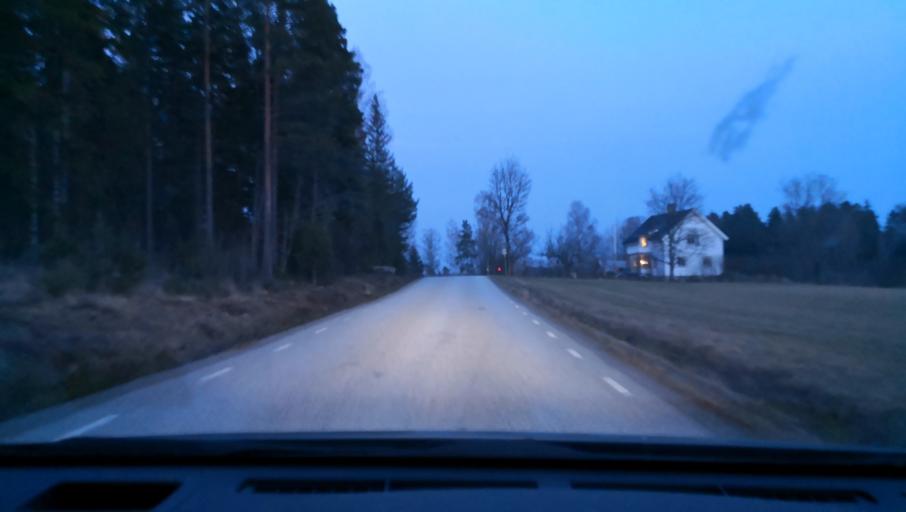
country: SE
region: OErebro
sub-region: Lindesbergs Kommun
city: Frovi
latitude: 59.5838
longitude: 15.4544
